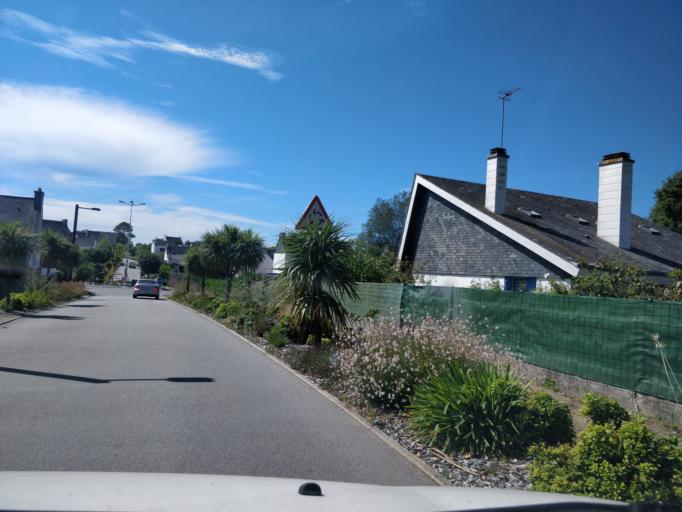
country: FR
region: Brittany
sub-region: Departement du Morbihan
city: Saint-Philibert
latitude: 47.5920
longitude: -2.9996
